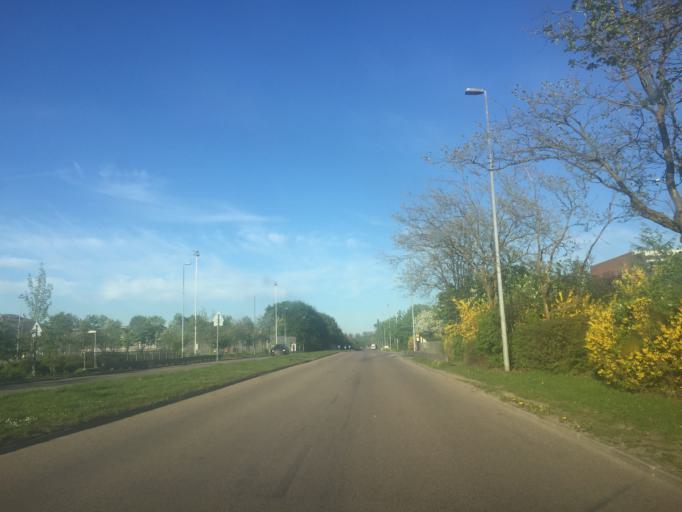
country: DK
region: Capital Region
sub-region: Hoje-Taastrup Kommune
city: Taastrup
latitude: 55.6516
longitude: 12.2712
